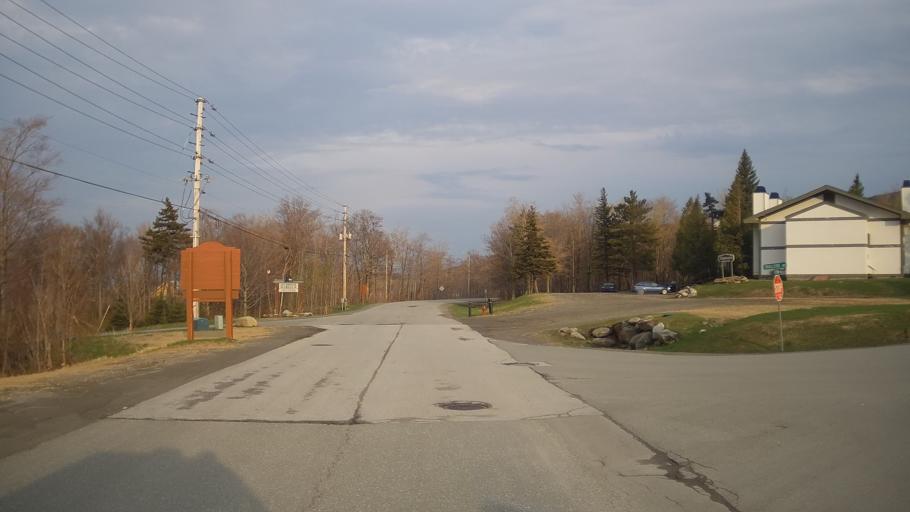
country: US
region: Vermont
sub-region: Franklin County
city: Richford
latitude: 44.9384
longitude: -72.5022
